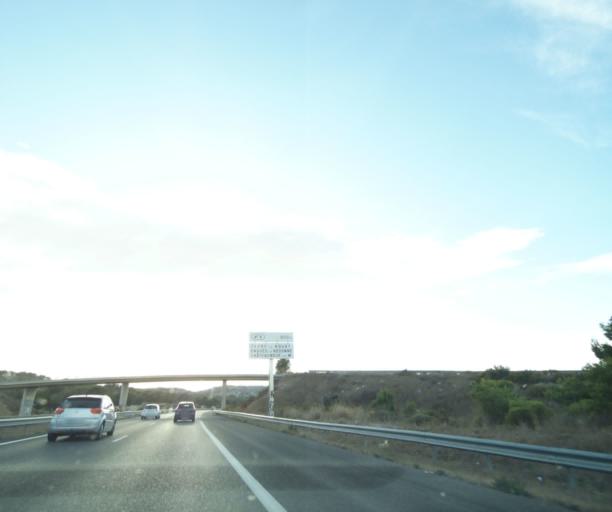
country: FR
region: Provence-Alpes-Cote d'Azur
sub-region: Departement des Bouches-du-Rhone
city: Ensues-la-Redonne
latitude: 43.3761
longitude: 5.1997
